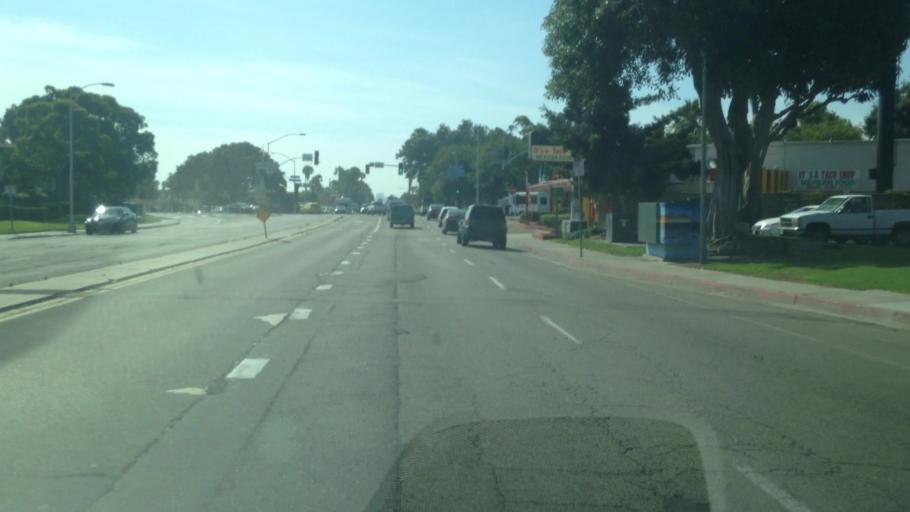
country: US
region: California
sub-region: San Diego County
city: San Diego
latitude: 32.7555
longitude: -117.2206
